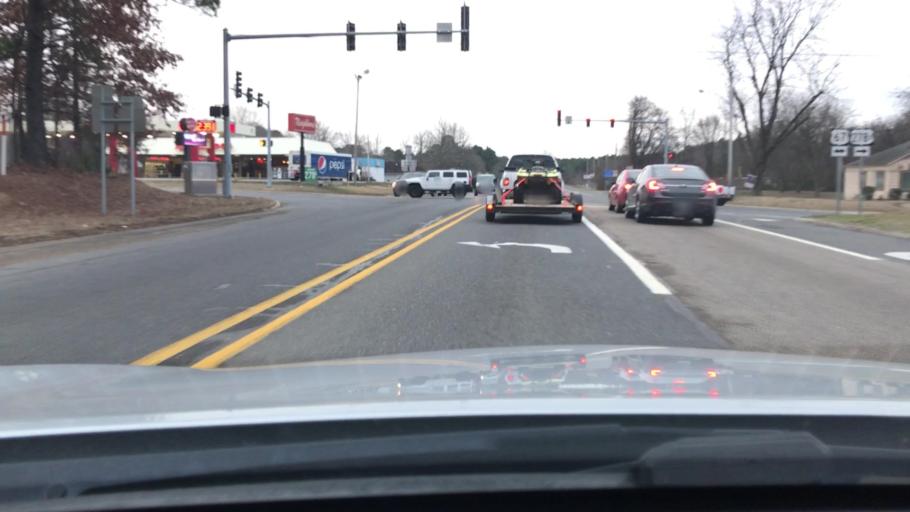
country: US
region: Arkansas
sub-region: Hempstead County
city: Hope
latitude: 33.6686
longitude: -93.5758
